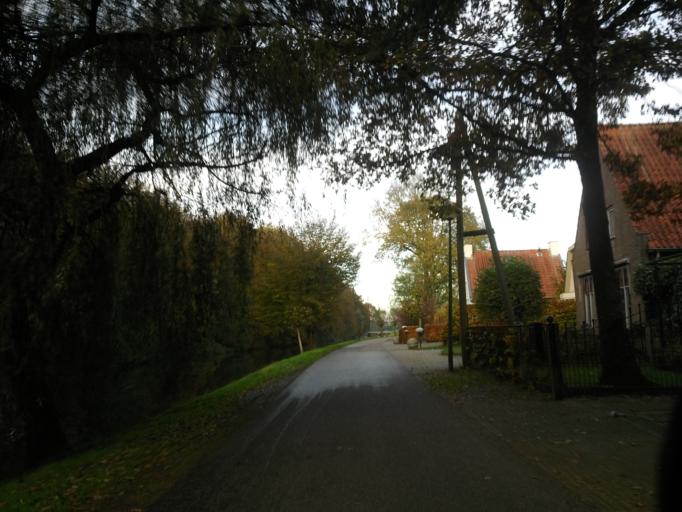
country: NL
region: Utrecht
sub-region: Gemeente Leusden
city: Leusden
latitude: 52.1326
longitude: 5.4469
